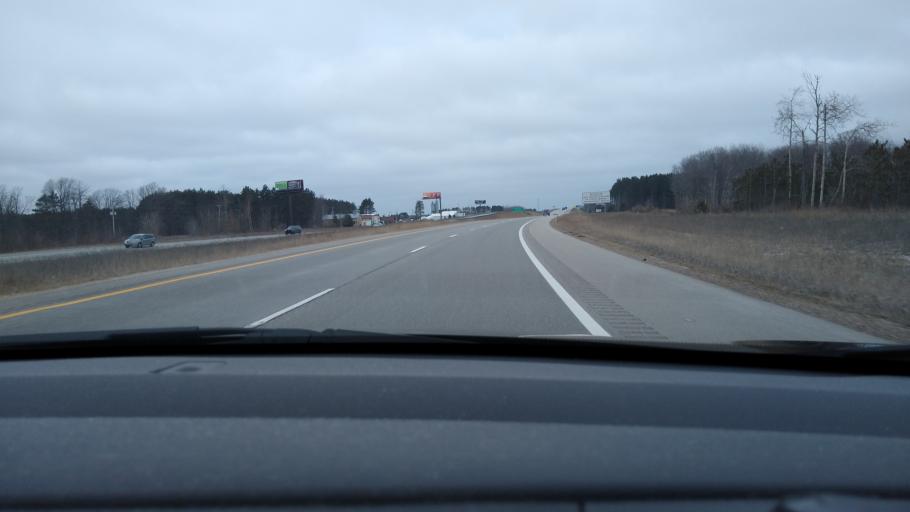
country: US
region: Michigan
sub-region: Otsego County
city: Gaylord
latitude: 44.9976
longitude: -84.6857
